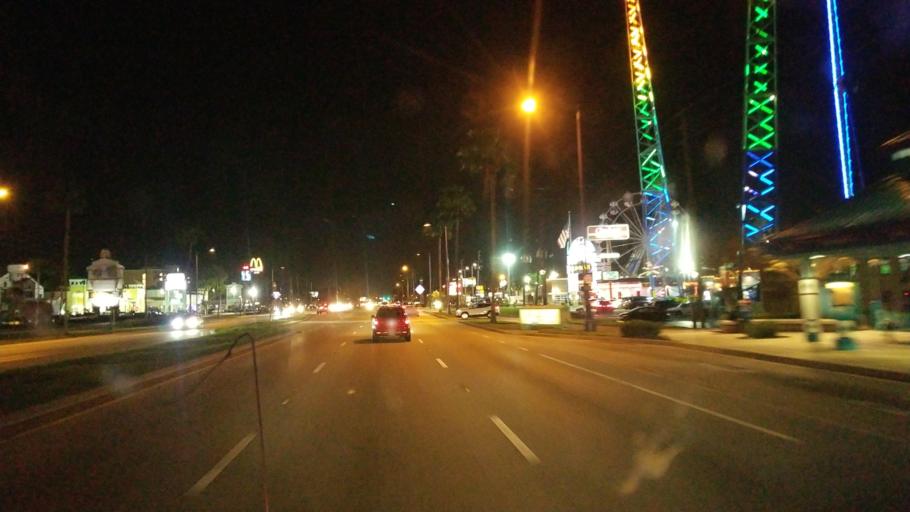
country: US
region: Florida
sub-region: Osceola County
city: Celebration
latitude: 28.3327
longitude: -81.5173
